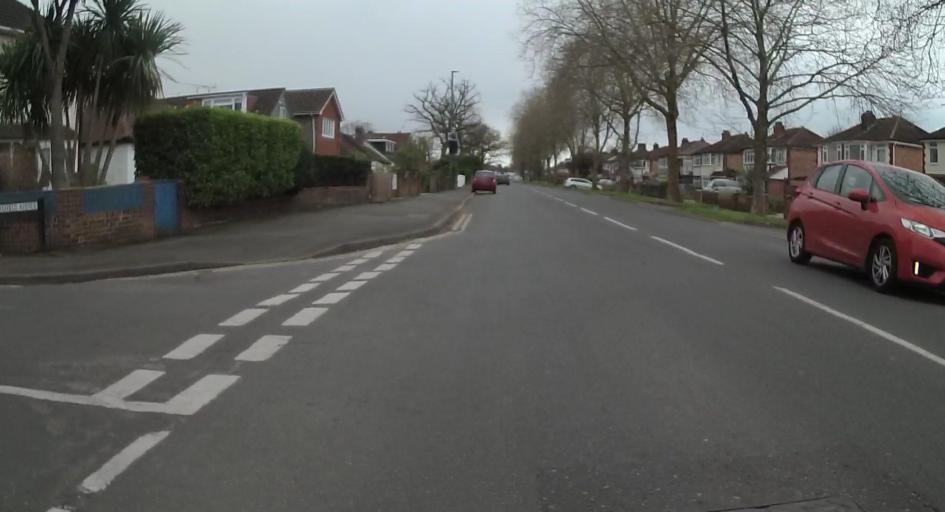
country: GB
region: England
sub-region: Surrey
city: West Byfleet
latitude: 51.3513
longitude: -0.4947
